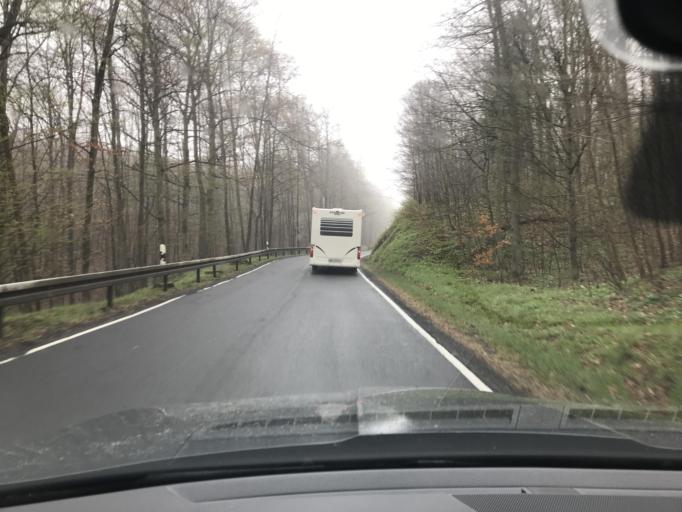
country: DE
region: Saxony-Anhalt
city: Harzgerode
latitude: 51.6604
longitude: 11.1414
